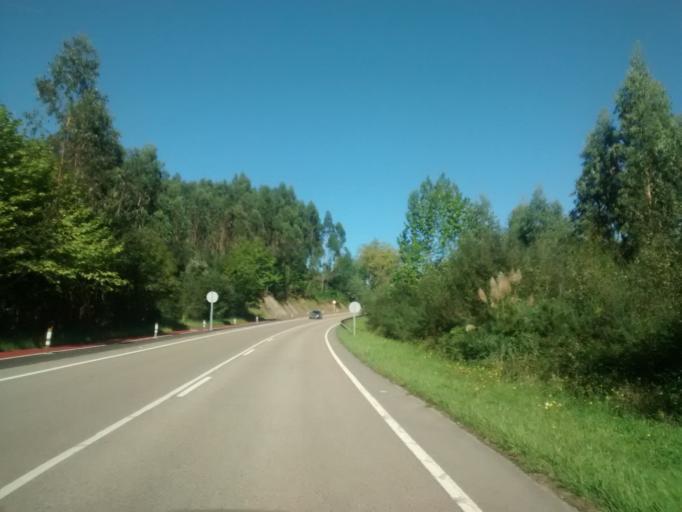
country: ES
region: Cantabria
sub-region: Provincia de Cantabria
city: Cabezon de la Sal
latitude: 43.3229
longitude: -4.2587
